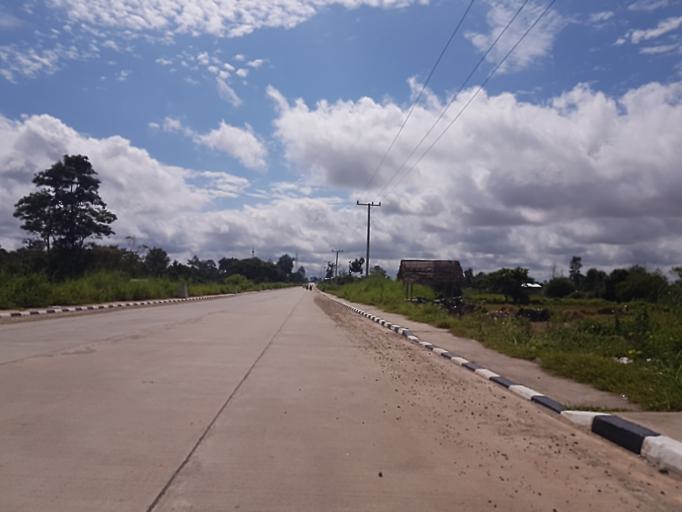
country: TH
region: Nong Khai
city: Nong Khai
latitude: 17.9124
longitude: 102.6963
